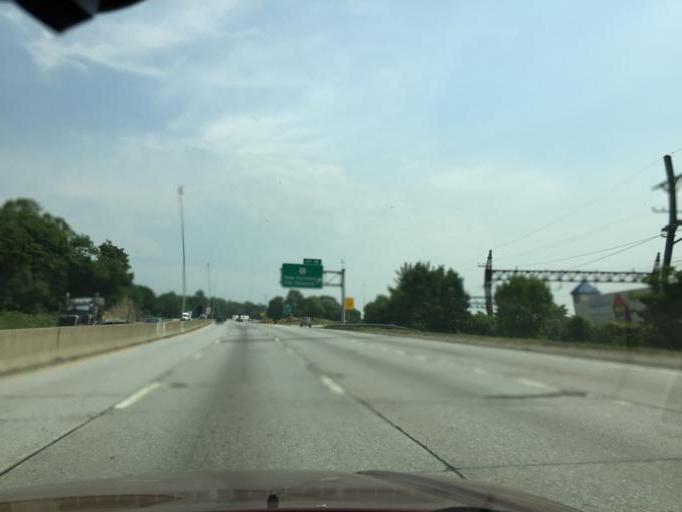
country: US
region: New York
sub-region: Westchester County
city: Pelham Manor
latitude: 40.8970
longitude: -73.7972
